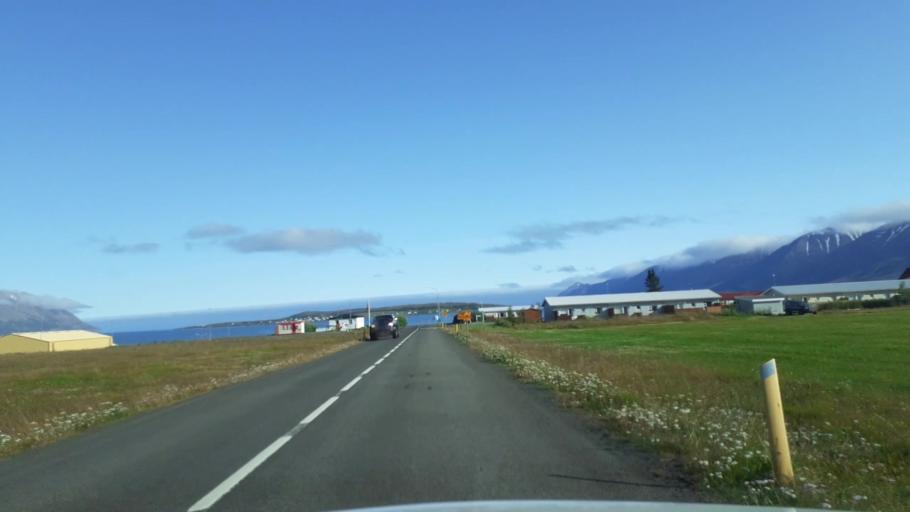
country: IS
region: Northeast
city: Dalvik
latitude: 65.9428
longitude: -18.3541
